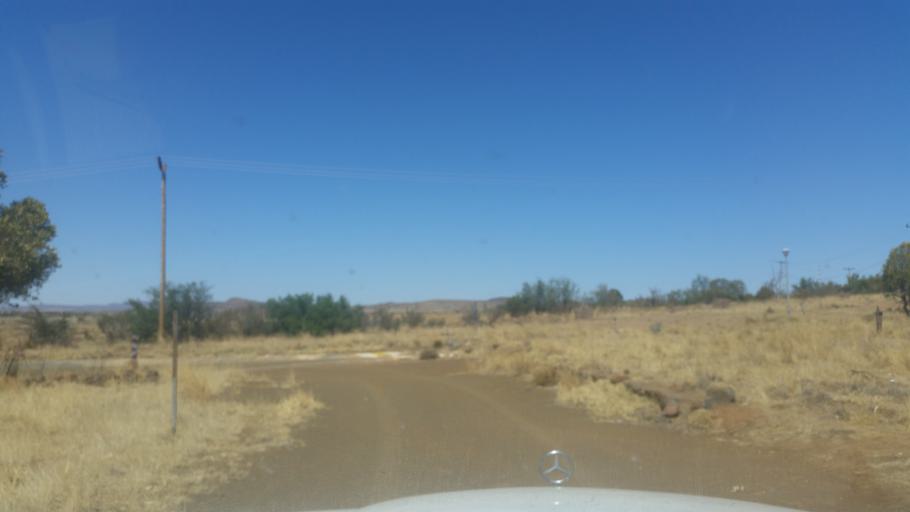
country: ZA
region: Eastern Cape
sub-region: Joe Gqabi District Municipality
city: Burgersdorp
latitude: -30.6926
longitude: 25.7771
